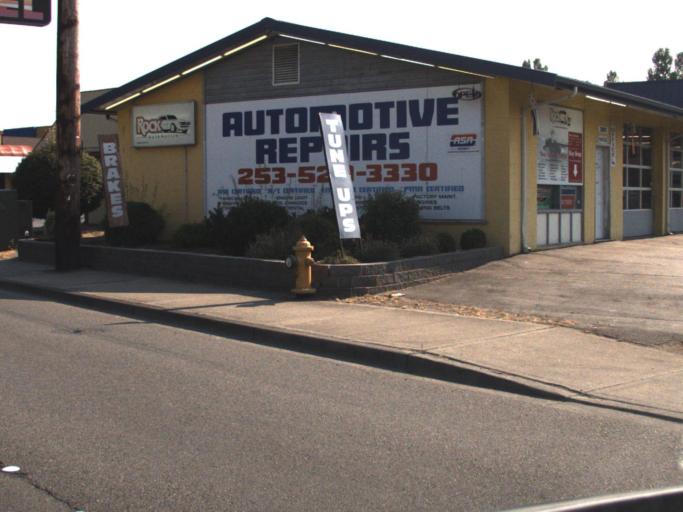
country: US
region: Washington
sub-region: King County
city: Des Moines
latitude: 47.3771
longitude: -122.2993
